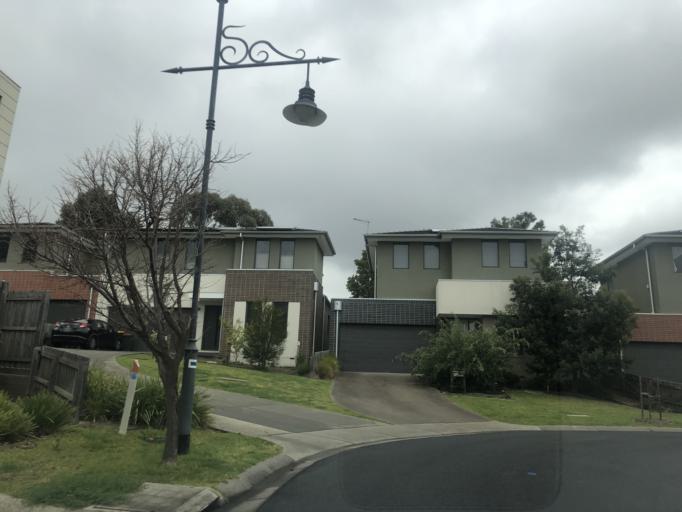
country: AU
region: Victoria
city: Burwood East
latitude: -37.8607
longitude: 145.1443
